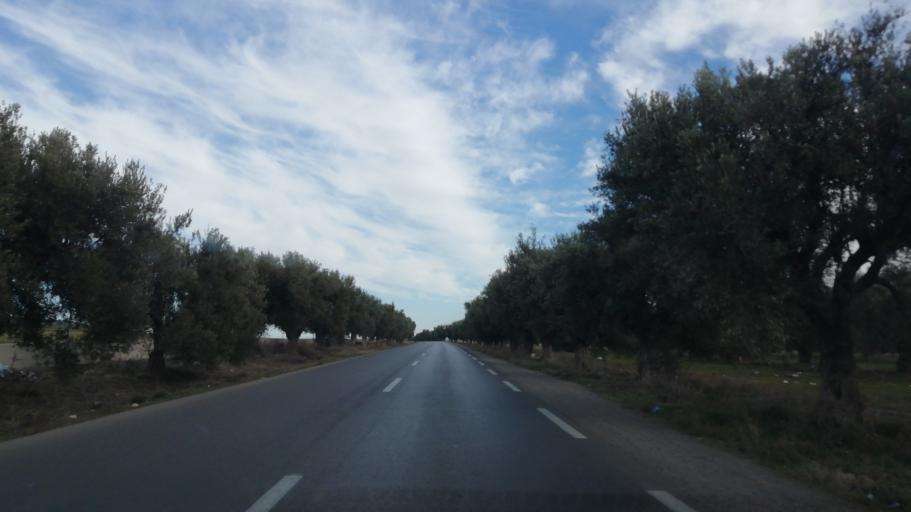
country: DZ
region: Sidi Bel Abbes
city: Sidi Bel Abbes
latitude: 35.1782
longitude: -0.4394
